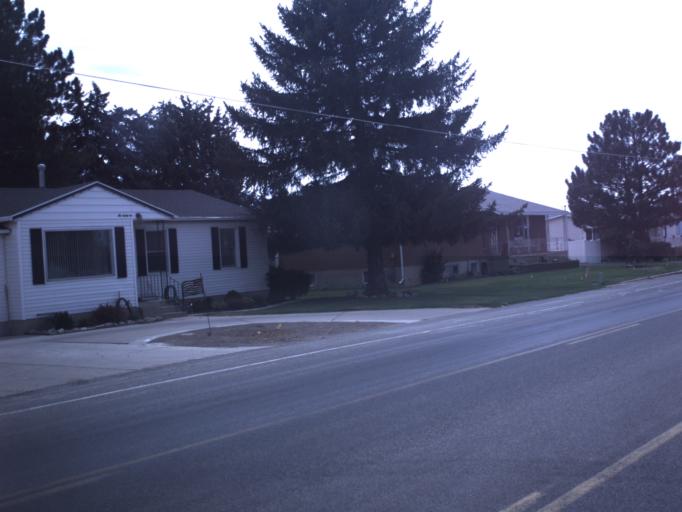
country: US
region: Utah
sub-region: Davis County
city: Syracuse
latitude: 41.0992
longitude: -112.0647
